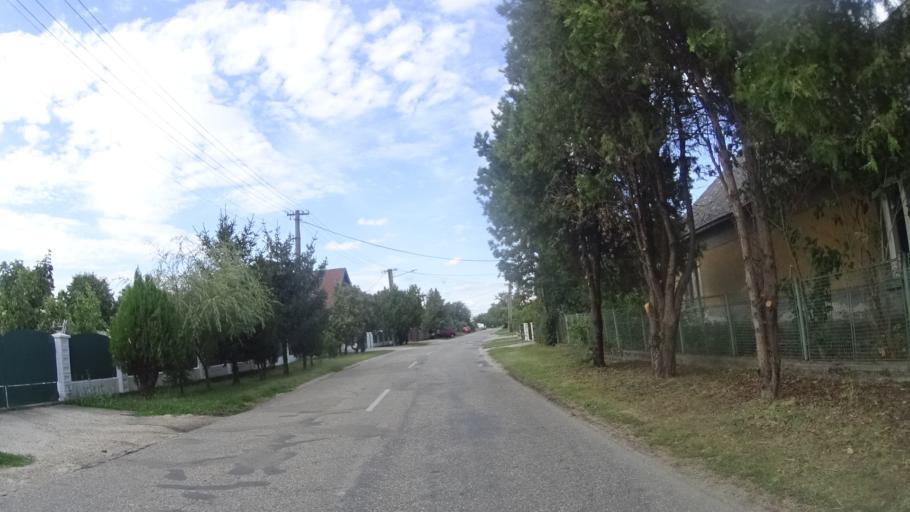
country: SK
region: Trnavsky
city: Gabcikovo
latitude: 47.9083
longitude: 17.5257
